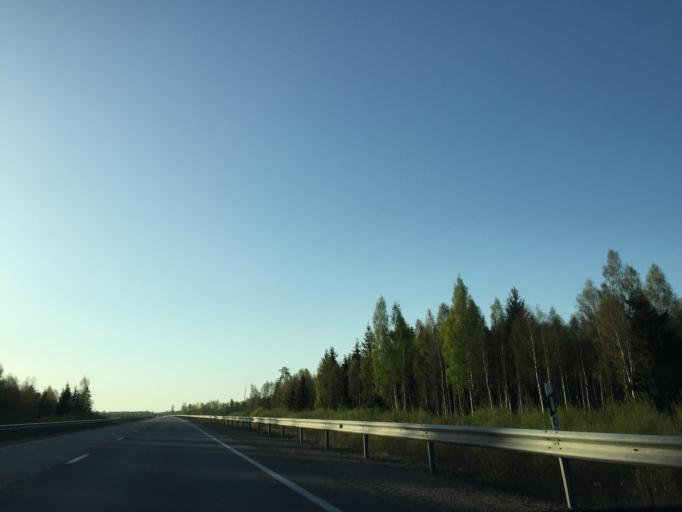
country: LV
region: Koknese
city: Koknese
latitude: 56.6784
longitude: 25.3883
